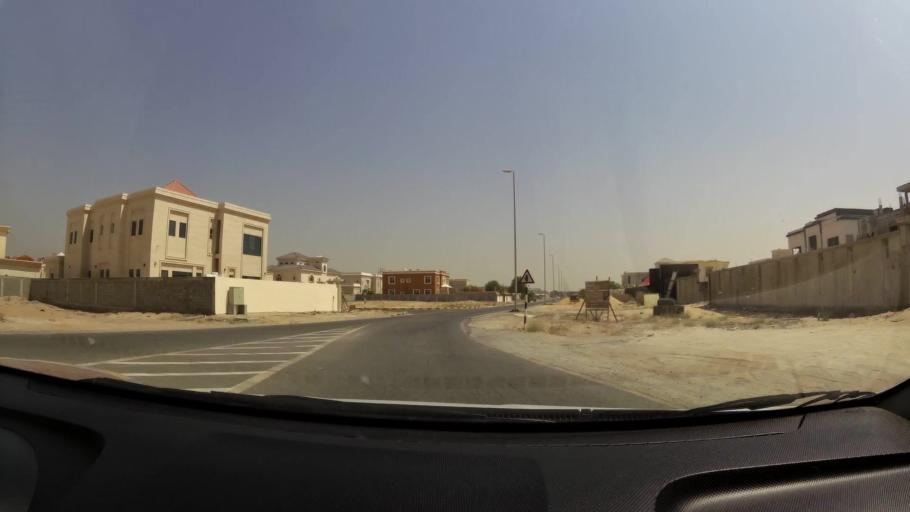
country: AE
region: Ajman
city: Ajman
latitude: 25.4167
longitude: 55.5209
